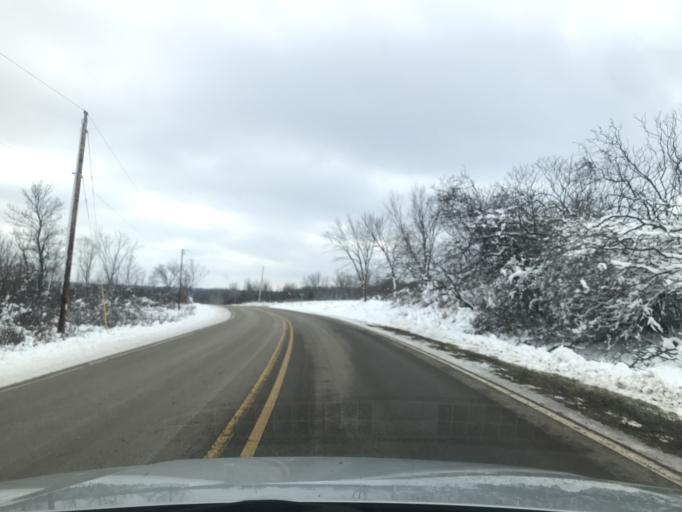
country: US
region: Wisconsin
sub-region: Oconto County
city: Oconto
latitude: 44.9337
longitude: -87.9885
